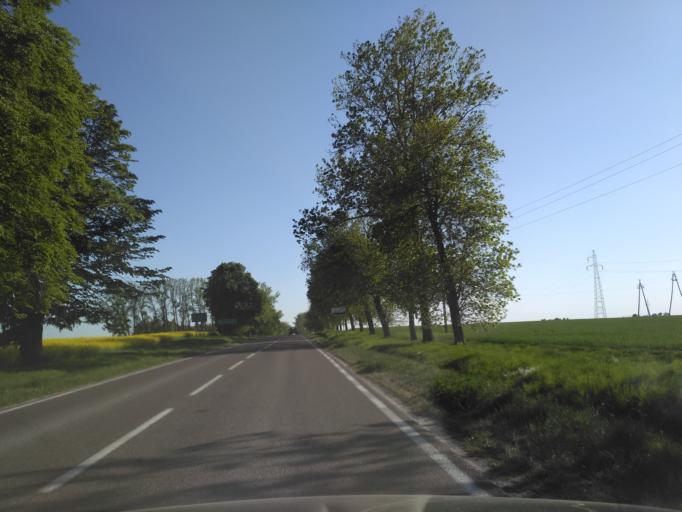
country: PL
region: Lublin Voivodeship
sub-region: Powiat leczynski
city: Cycow
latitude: 51.2279
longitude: 23.0809
